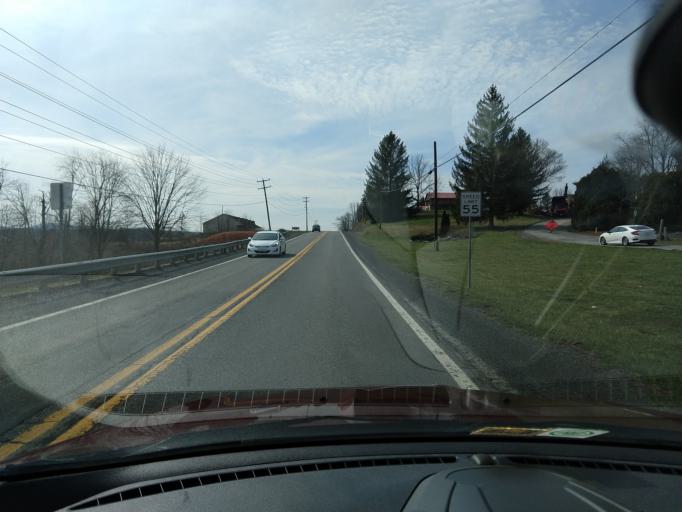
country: US
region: West Virginia
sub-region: Greenbrier County
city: Lewisburg
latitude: 37.8433
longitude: -80.4149
